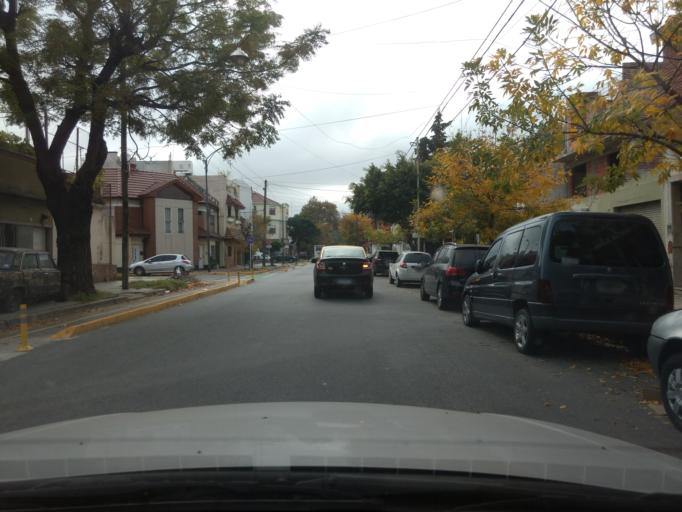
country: AR
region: Buenos Aires F.D.
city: Villa Santa Rita
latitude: -34.6146
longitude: -58.5070
